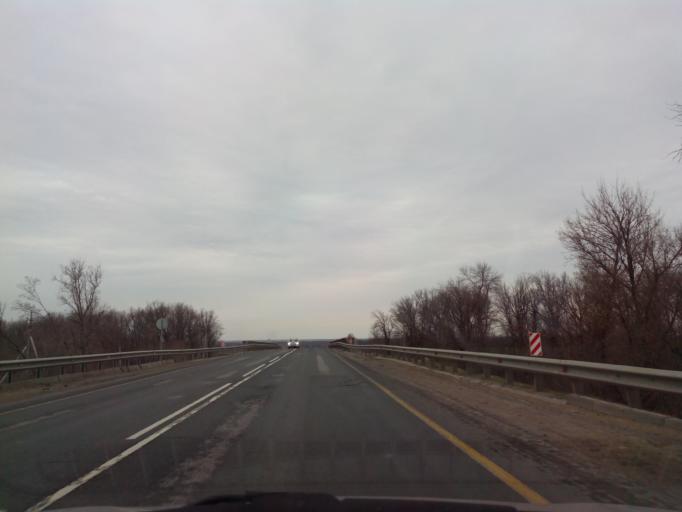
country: RU
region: Tambov
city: Zavoronezhskoye
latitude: 52.9163
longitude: 40.6268
